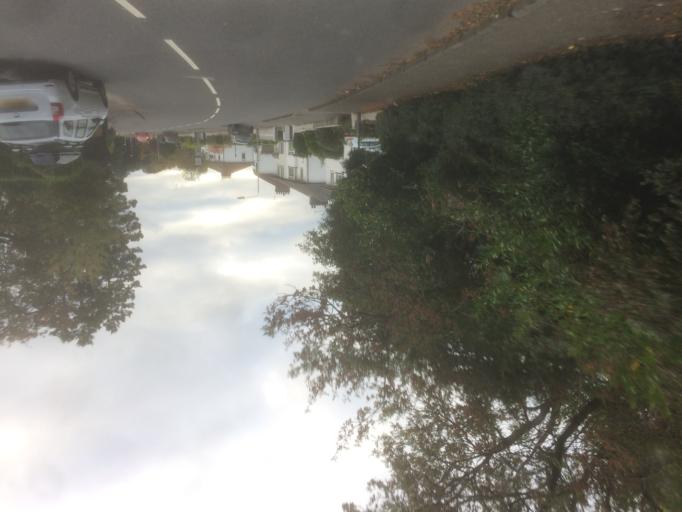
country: GB
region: Scotland
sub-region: East Renfrewshire
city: Giffnock
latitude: 55.8049
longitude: -4.3068
